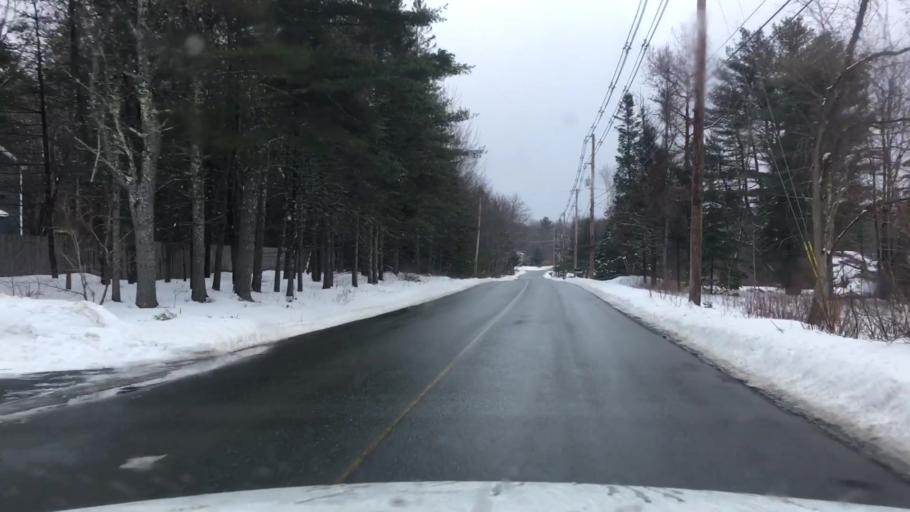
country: US
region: Maine
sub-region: Hancock County
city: Trenton
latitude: 44.4141
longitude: -68.3346
